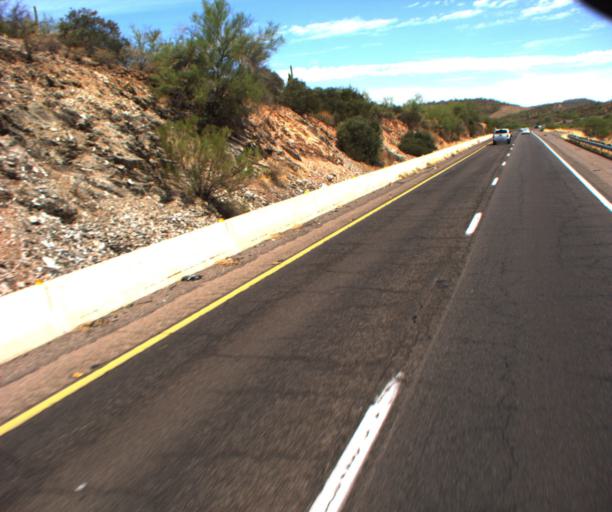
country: US
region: Arizona
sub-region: Maricopa County
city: New River
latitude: 33.9364
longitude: -112.1402
